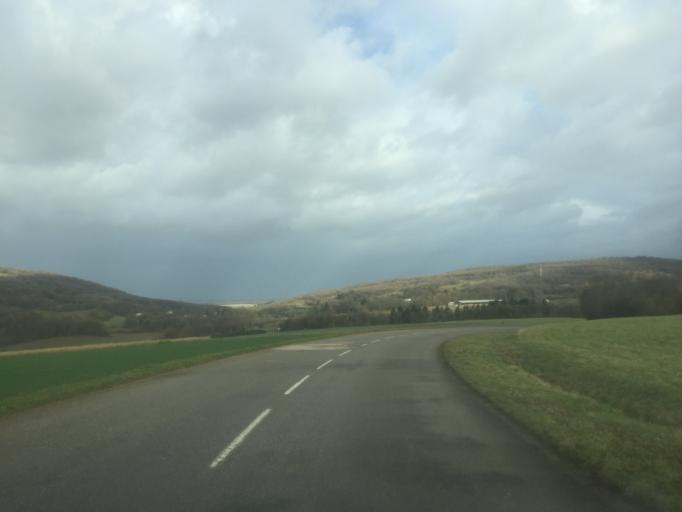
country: FR
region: Franche-Comte
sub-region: Departement du Jura
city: Orchamps
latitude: 47.2120
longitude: 5.6825
